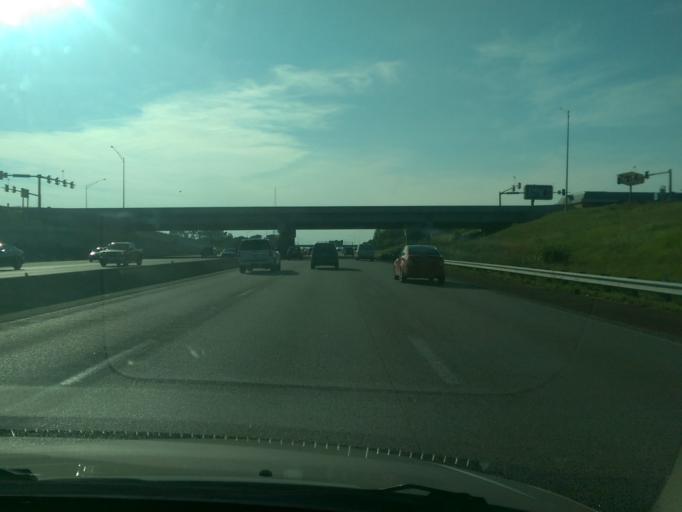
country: US
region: Missouri
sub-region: Jackson County
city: Raytown
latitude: 39.0514
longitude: -94.4733
